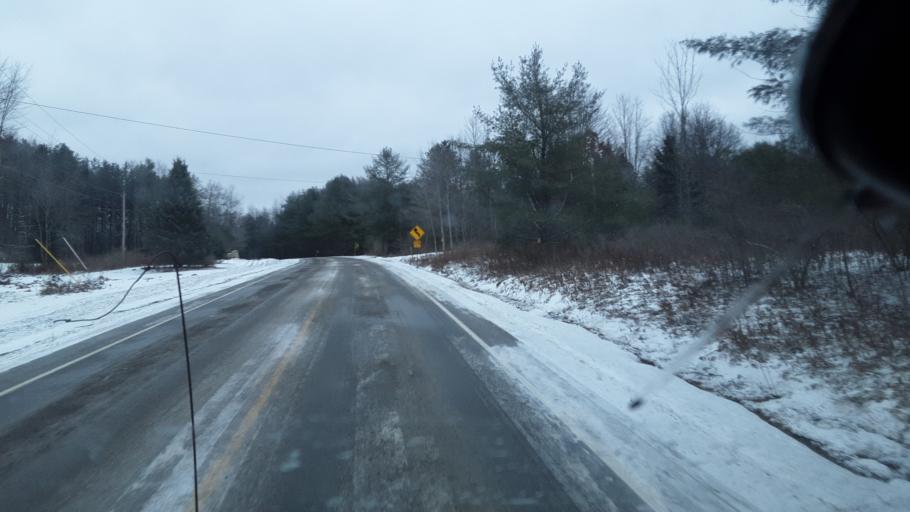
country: US
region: New York
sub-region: Allegany County
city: Friendship
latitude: 42.2263
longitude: -78.1404
